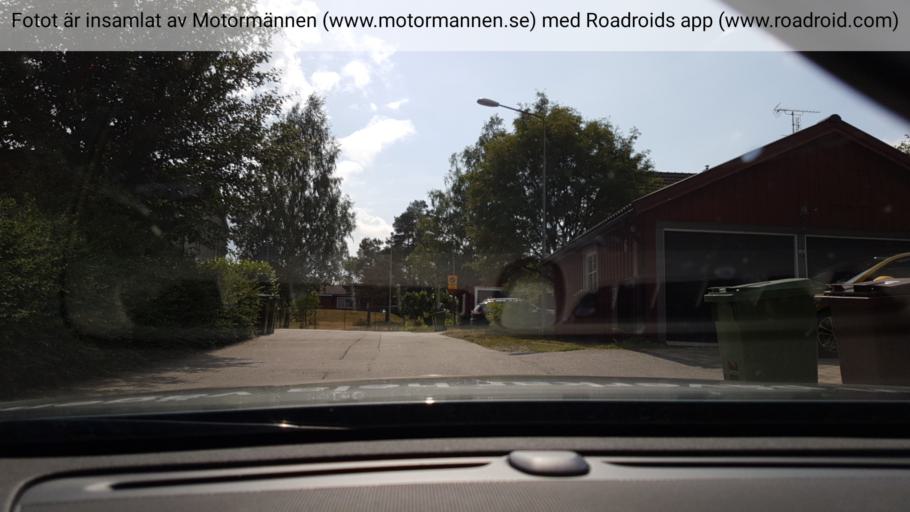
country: SE
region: Vaesterbotten
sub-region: Umea Kommun
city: Umea
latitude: 63.8233
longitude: 20.2383
